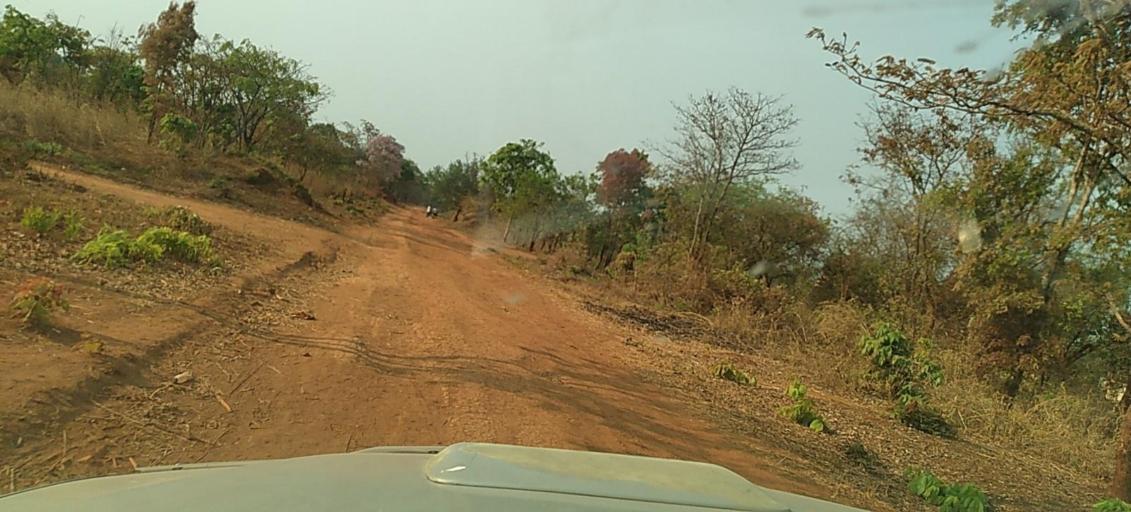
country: ZM
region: North-Western
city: Kasempa
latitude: -13.2969
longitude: 26.5543
